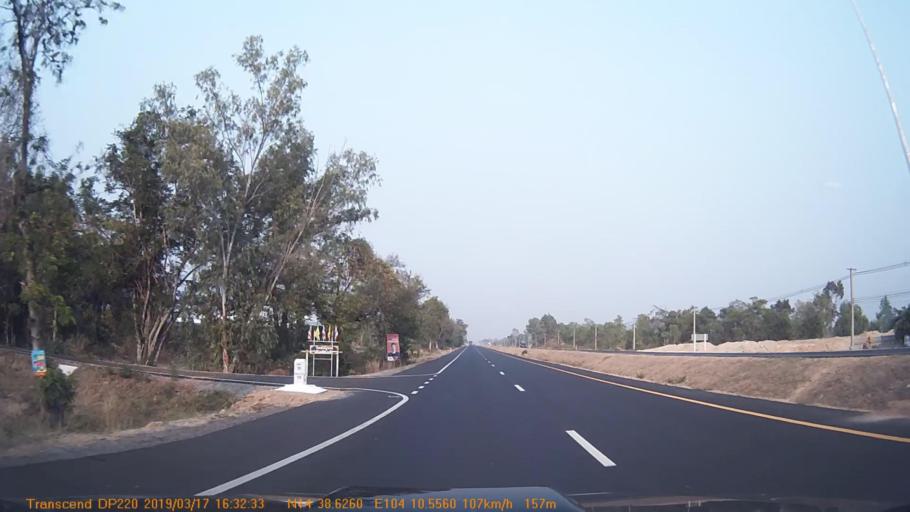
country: TH
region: Sisaket
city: Khu Khan
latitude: 14.6438
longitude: 104.1762
